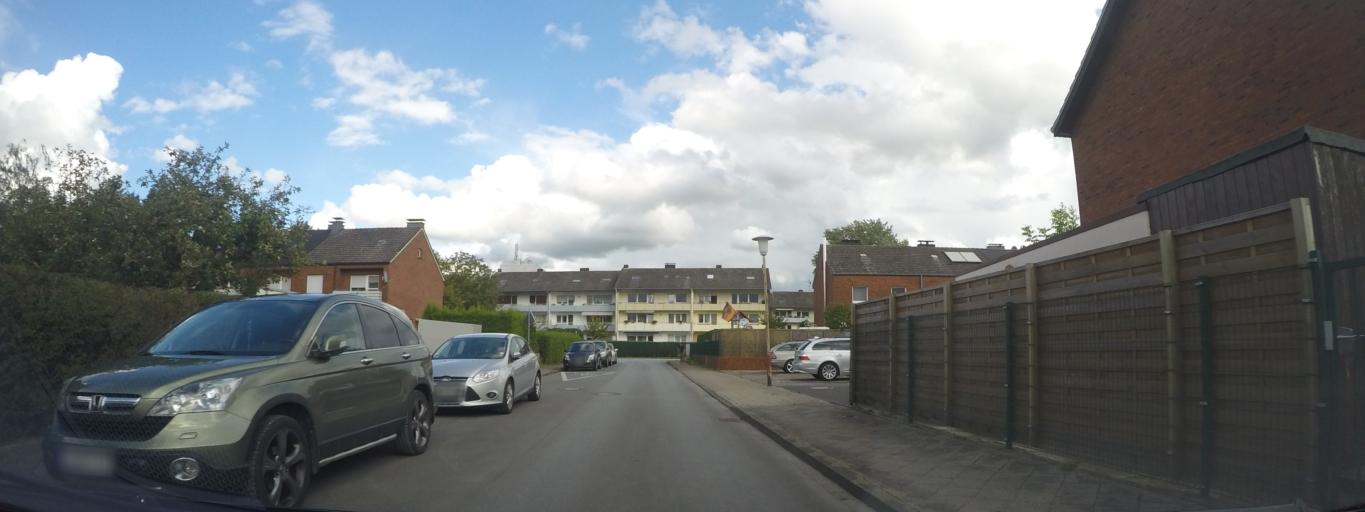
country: DE
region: North Rhine-Westphalia
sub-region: Regierungsbezirk Arnsberg
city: Lippstadt
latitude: 51.6885
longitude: 8.3392
